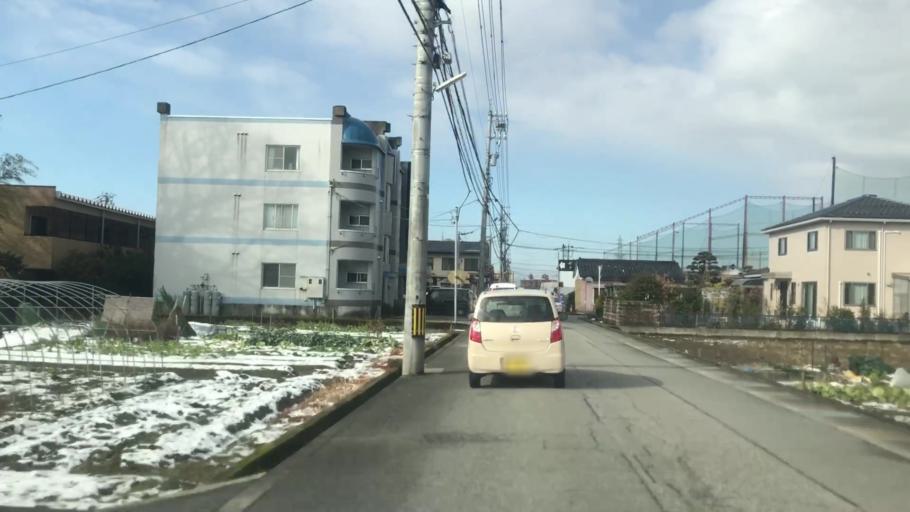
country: JP
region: Toyama
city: Toyama-shi
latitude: 36.6612
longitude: 137.2188
